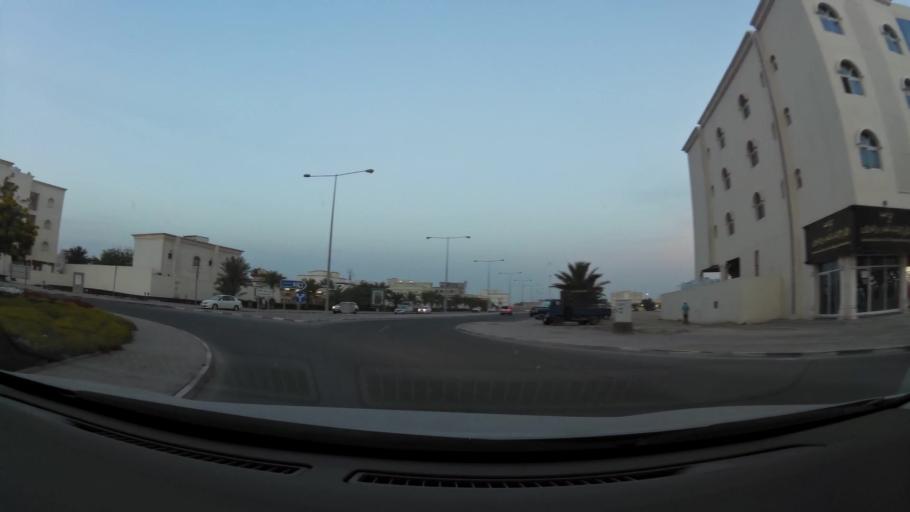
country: QA
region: Al Wakrah
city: Al Wakrah
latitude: 25.1513
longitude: 51.5987
